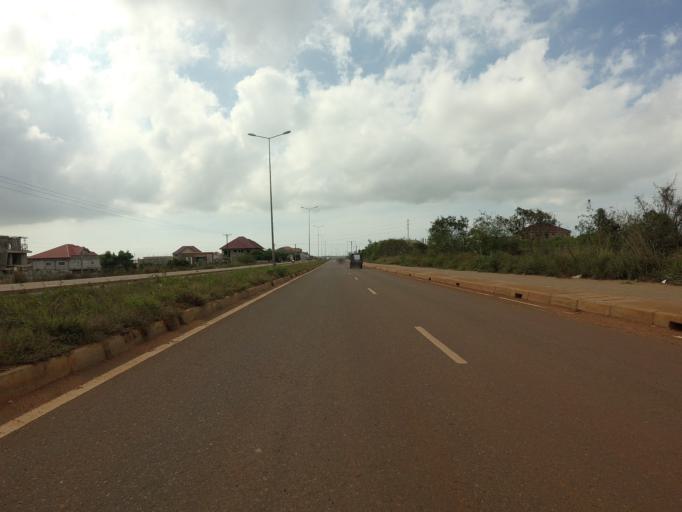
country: GH
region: Greater Accra
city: Teshi Old Town
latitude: 5.6040
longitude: -0.1383
